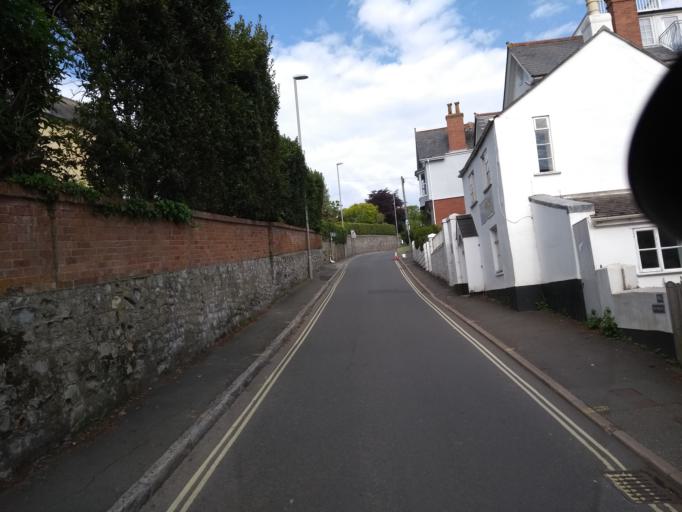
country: GB
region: England
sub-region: Dorset
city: Lyme Regis
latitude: 50.7256
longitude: -2.9376
